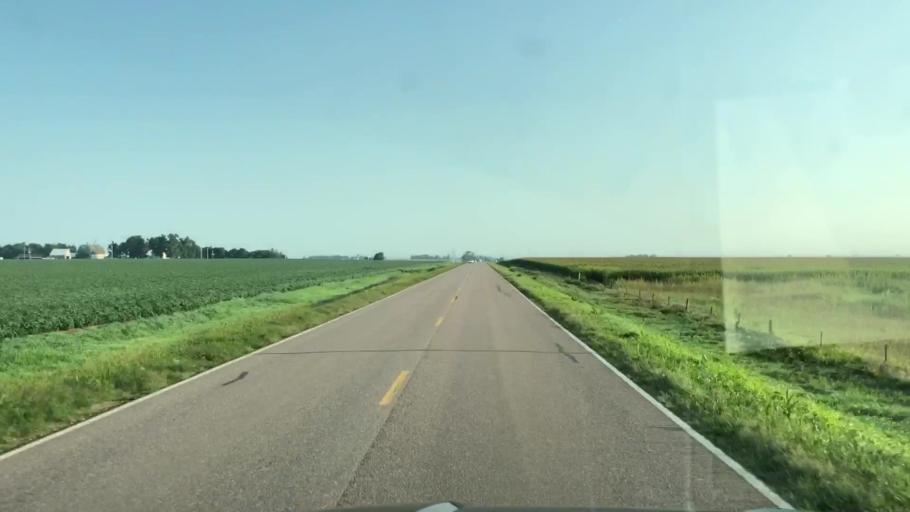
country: US
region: Iowa
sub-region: Lyon County
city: George
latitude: 43.2100
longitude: -96.0006
